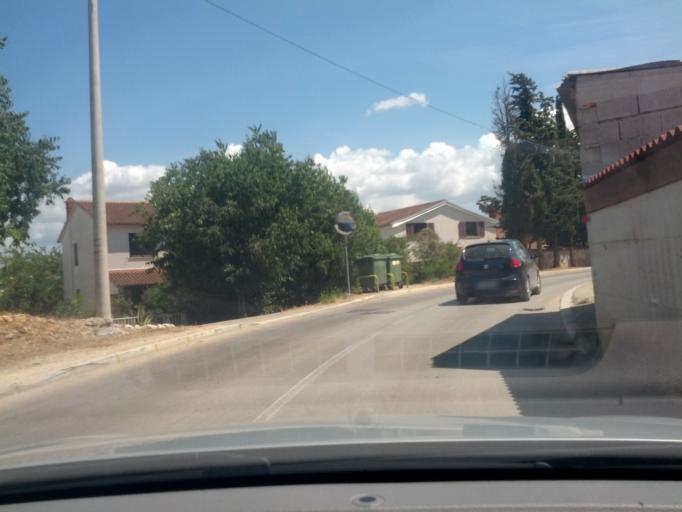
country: HR
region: Istarska
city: Fazana
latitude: 44.9529
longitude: 13.7969
